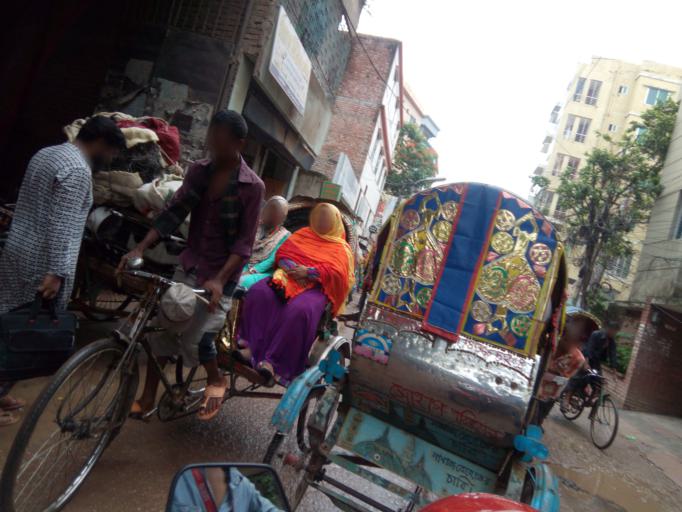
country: BD
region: Dhaka
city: Azimpur
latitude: 23.7586
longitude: 90.3596
